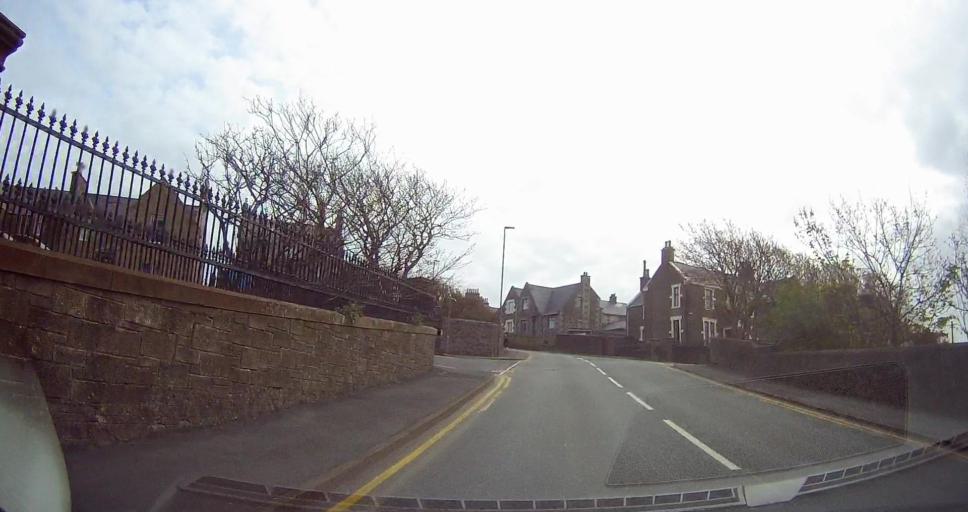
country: GB
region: Scotland
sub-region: Shetland Islands
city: Shetland
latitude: 60.1519
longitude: -1.1476
